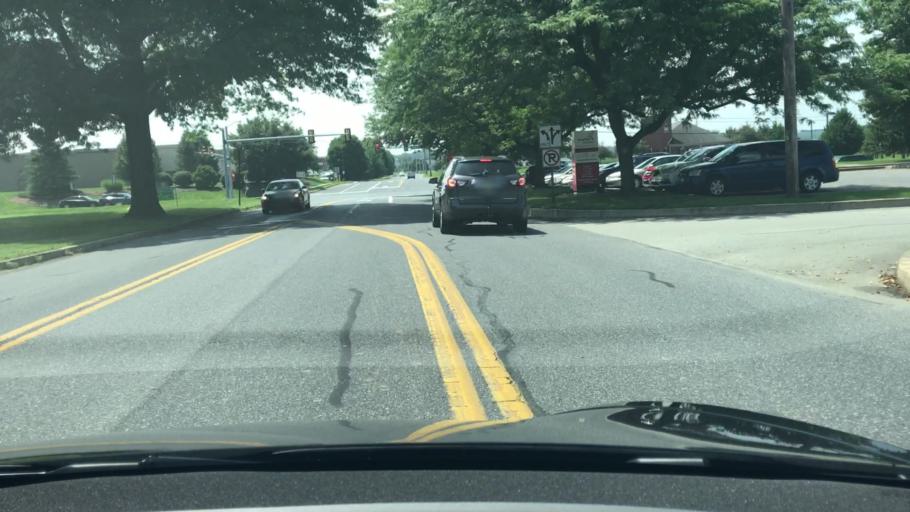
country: US
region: Pennsylvania
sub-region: Lancaster County
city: Landisville
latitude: 40.0681
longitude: -76.4124
